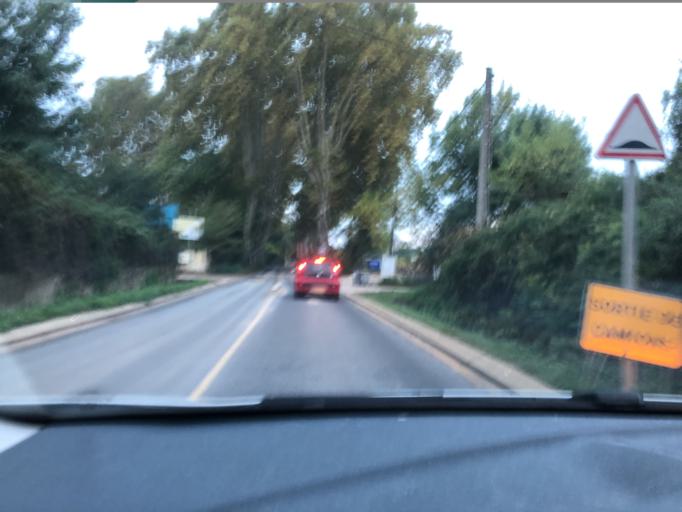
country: FR
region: Languedoc-Roussillon
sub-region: Departement de l'Herault
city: Montferrier-sur-Lez
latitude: 43.6628
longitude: 3.8629
